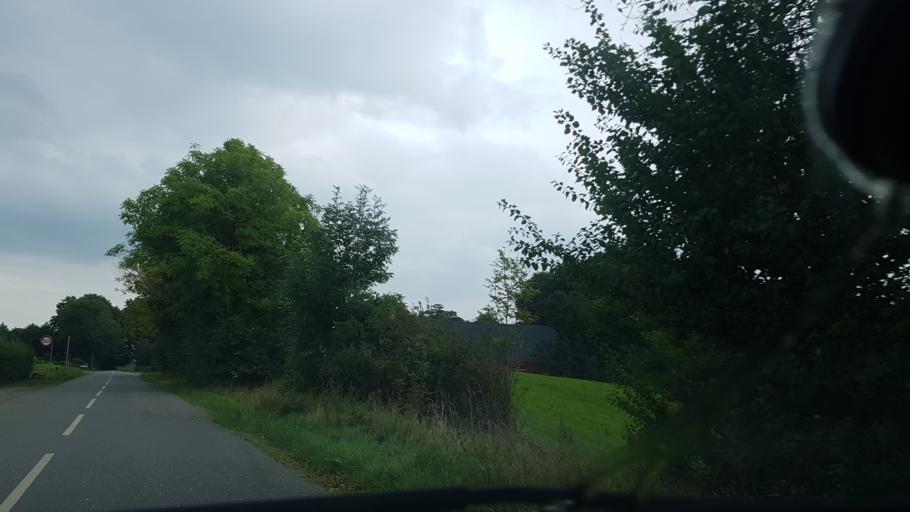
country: DK
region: South Denmark
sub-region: Kolding Kommune
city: Lunderskov
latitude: 55.5281
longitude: 9.3457
